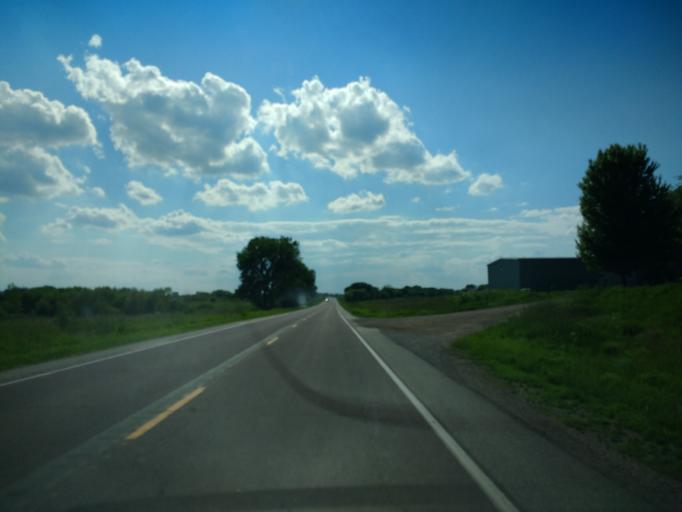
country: US
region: Iowa
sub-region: Clay County
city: Spencer
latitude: 43.1840
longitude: -95.1809
